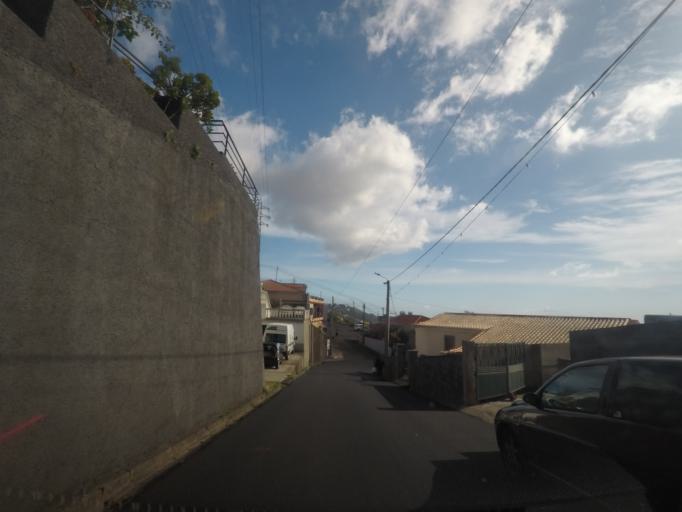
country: PT
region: Madeira
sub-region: Funchal
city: Nossa Senhora do Monte
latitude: 32.6746
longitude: -16.8926
